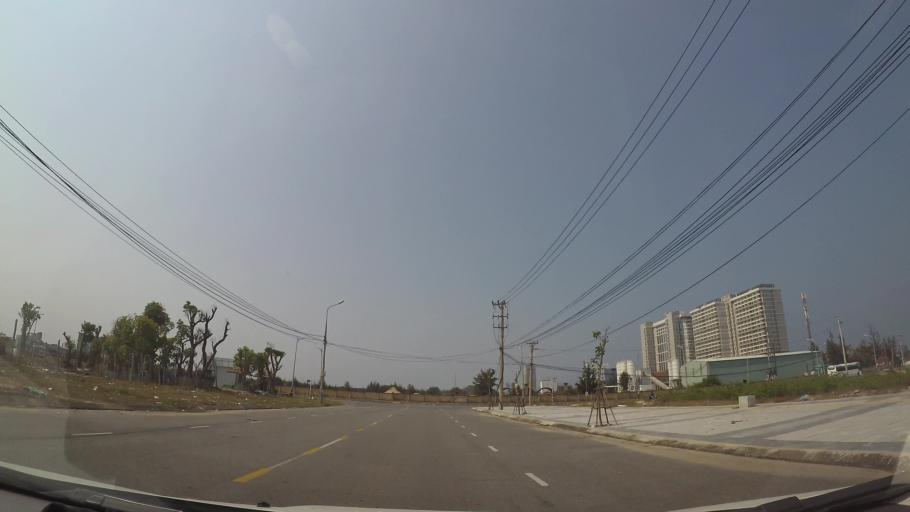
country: VN
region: Da Nang
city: Ngu Hanh Son
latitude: 16.0202
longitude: 108.2564
